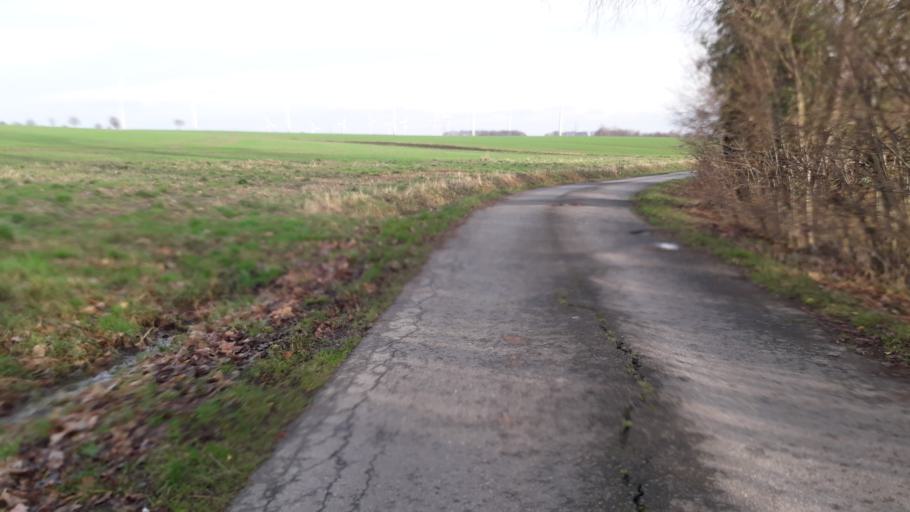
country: DE
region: North Rhine-Westphalia
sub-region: Regierungsbezirk Arnsberg
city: Welver
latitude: 51.5645
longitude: 7.9759
